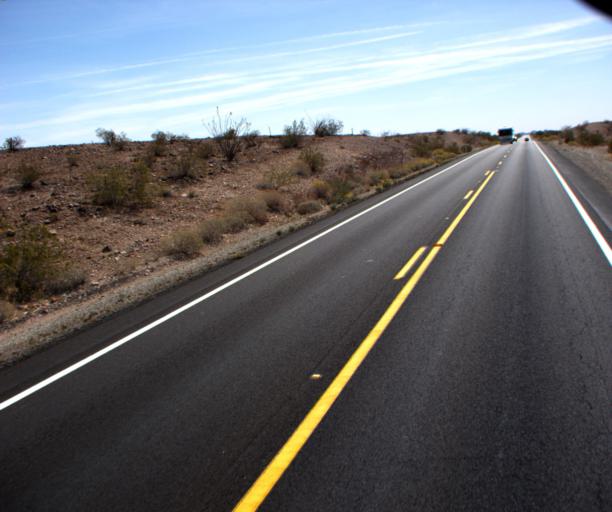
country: US
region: Arizona
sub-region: La Paz County
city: Quartzsite
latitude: 33.1616
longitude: -114.2794
